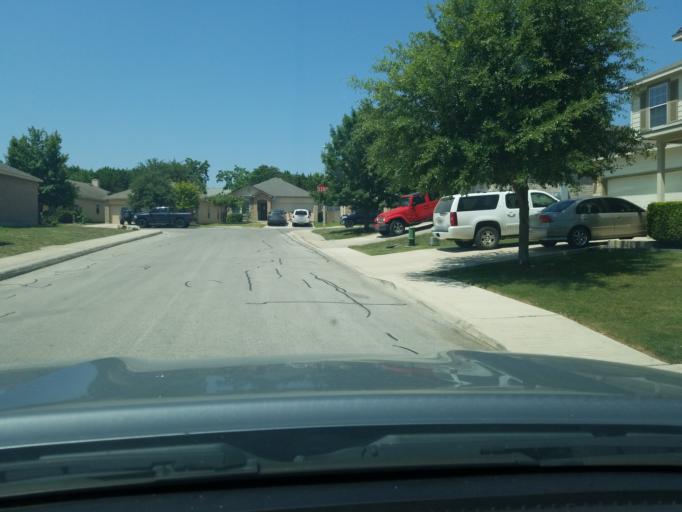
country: US
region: Texas
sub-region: Bexar County
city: Timberwood Park
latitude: 29.7005
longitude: -98.4838
